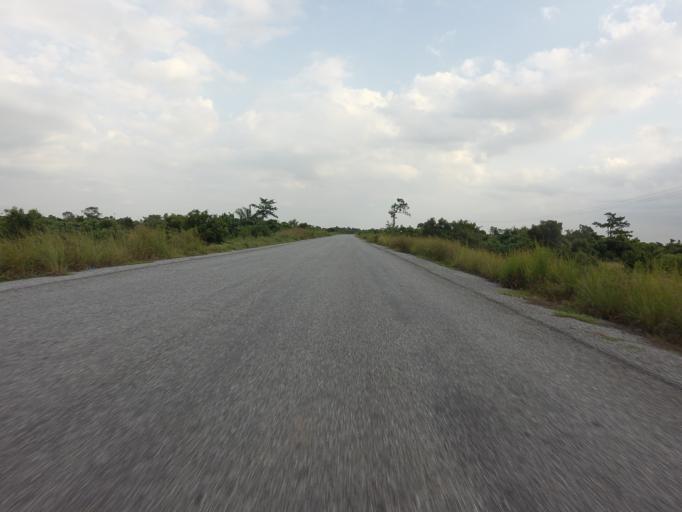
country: GH
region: Volta
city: Ho
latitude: 6.3804
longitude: 0.5318
